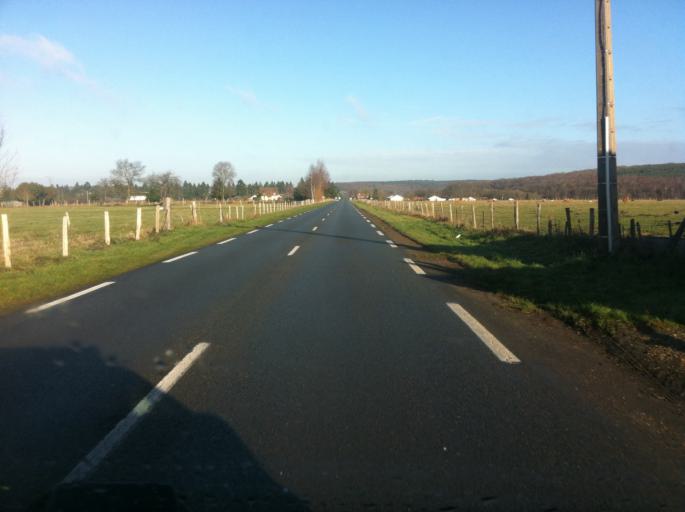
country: FR
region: Haute-Normandie
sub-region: Departement de la Seine-Maritime
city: Yainville
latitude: 49.4437
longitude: 0.8269
